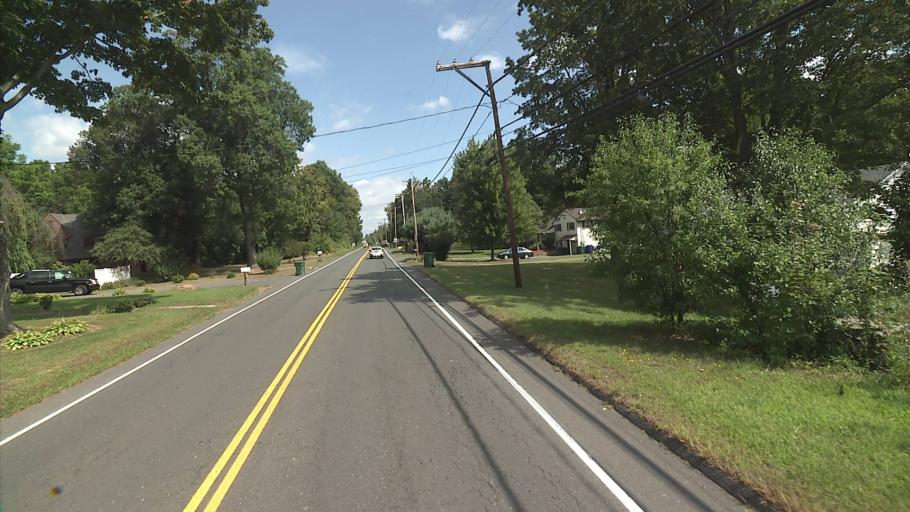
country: US
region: Connecticut
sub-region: Hartford County
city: Blue Hills
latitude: 41.8204
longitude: -72.7387
